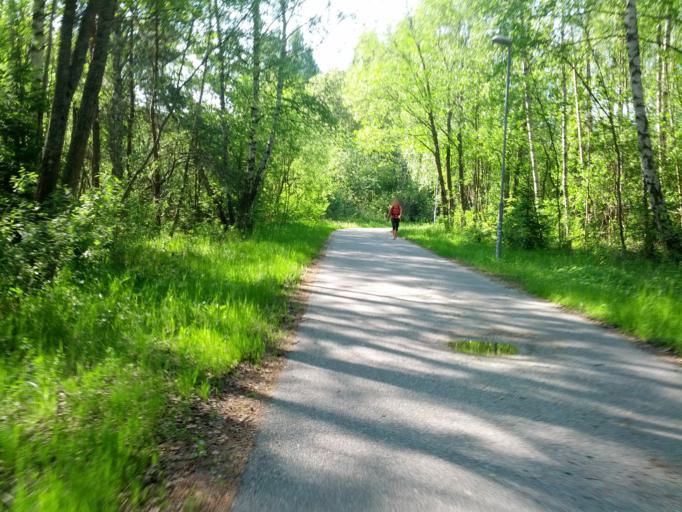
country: SE
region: Stockholm
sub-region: Danderyds Kommun
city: Djursholm
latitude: 59.4183
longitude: 18.0501
